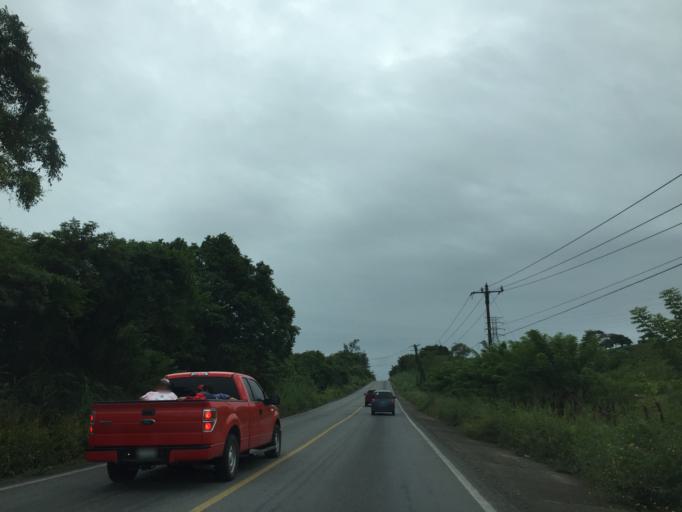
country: MX
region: Veracruz
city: Coatzintla
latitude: 20.4534
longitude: -97.4121
